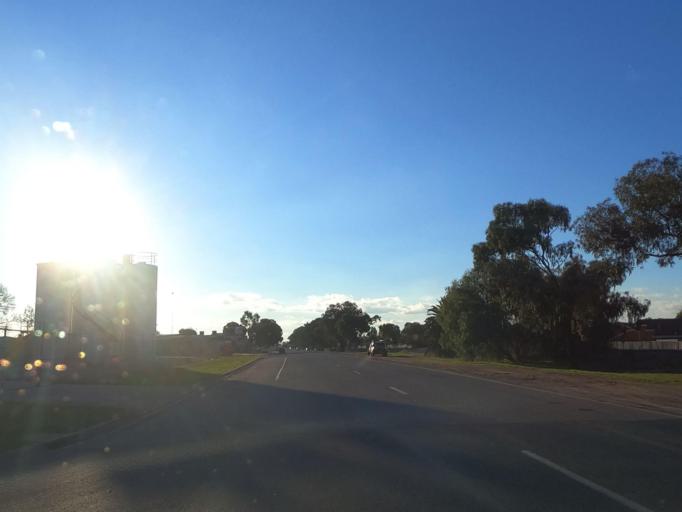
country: AU
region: Victoria
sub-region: Swan Hill
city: Swan Hill
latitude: -35.3336
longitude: 143.5591
